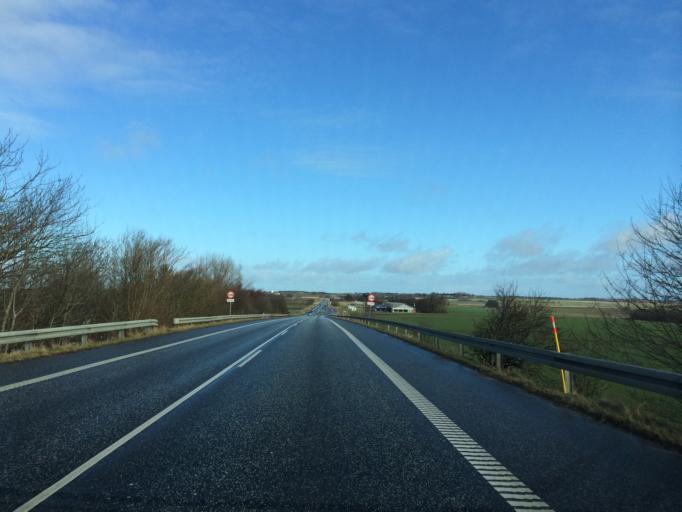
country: DK
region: Central Jutland
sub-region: Holstebro Kommune
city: Ulfborg
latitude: 56.2797
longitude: 8.3274
